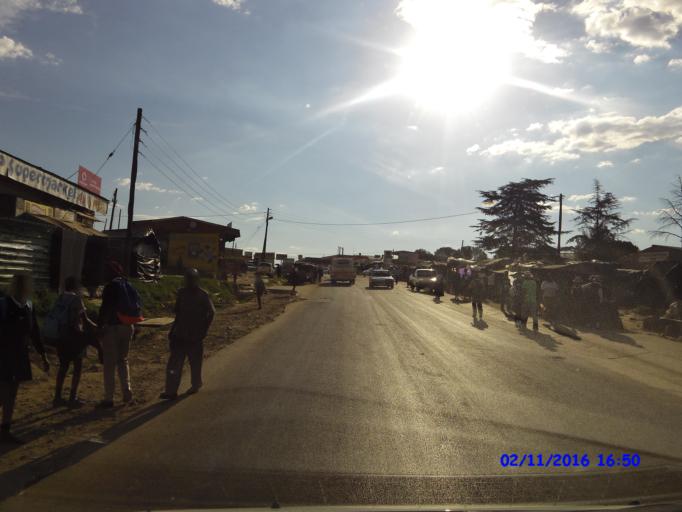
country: LS
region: Butha-Buthe
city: Butha-Buthe
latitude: -28.7678
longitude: 28.2512
